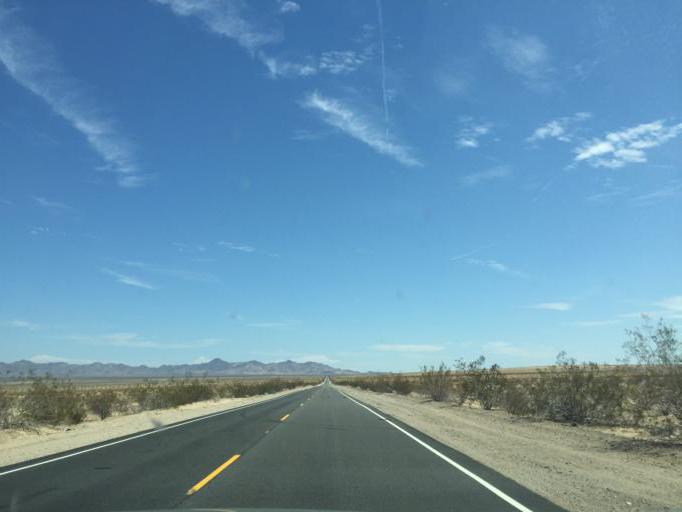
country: US
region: California
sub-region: Riverside County
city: Mesa Verde
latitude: 34.1005
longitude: -114.9975
